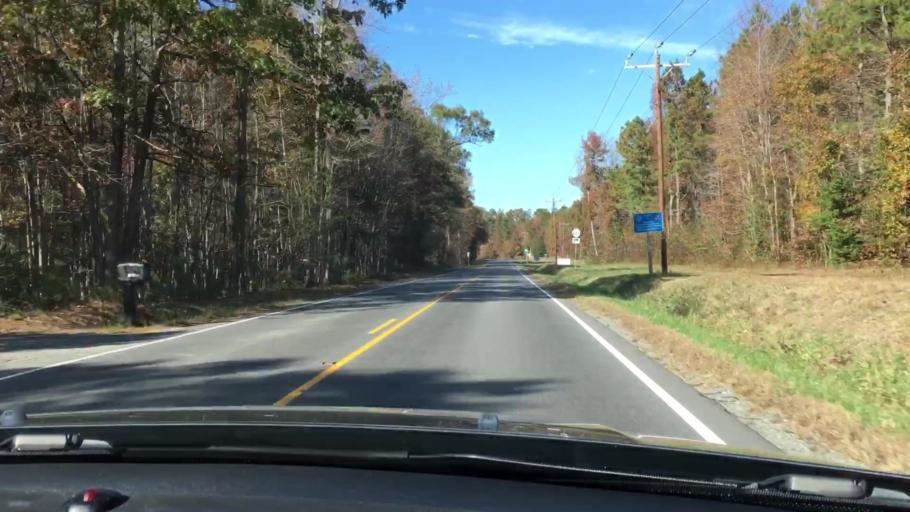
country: US
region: Virginia
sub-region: King and Queen County
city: King and Queen Court House
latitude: 37.6468
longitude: -76.9412
